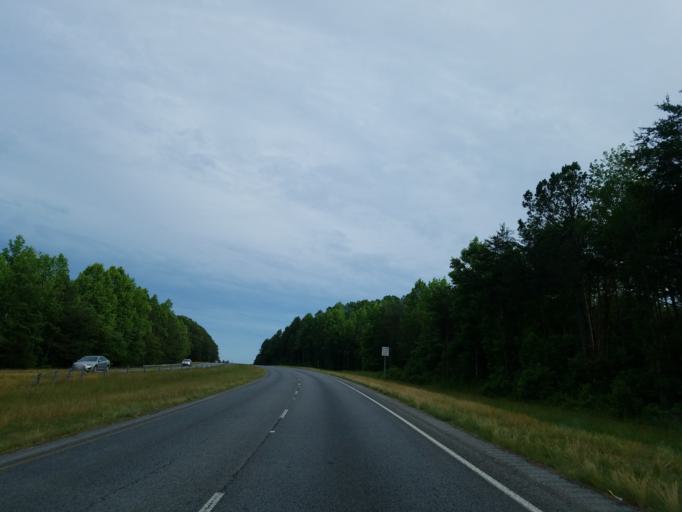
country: US
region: Georgia
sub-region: Lumpkin County
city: Dahlonega
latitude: 34.4348
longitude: -83.9940
